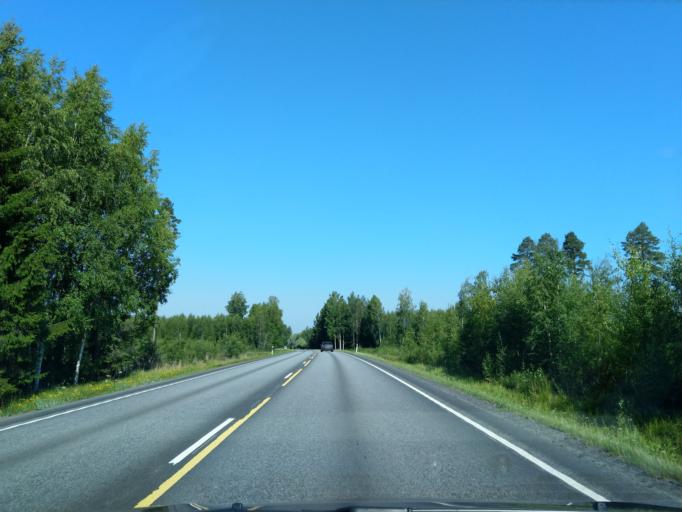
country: FI
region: Satakunta
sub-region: Pori
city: Huittinen
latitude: 61.1619
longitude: 22.7185
